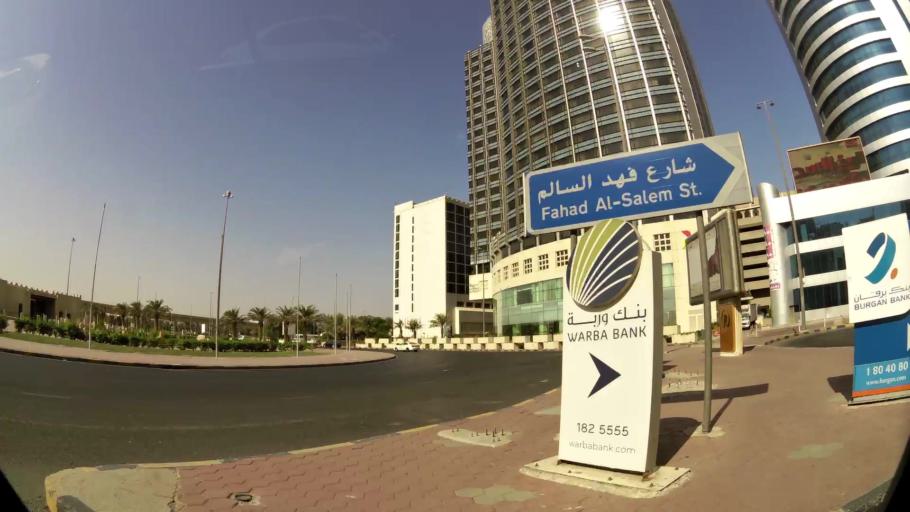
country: KW
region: Al Asimah
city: Ash Shamiyah
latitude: 29.3613
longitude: 47.9643
